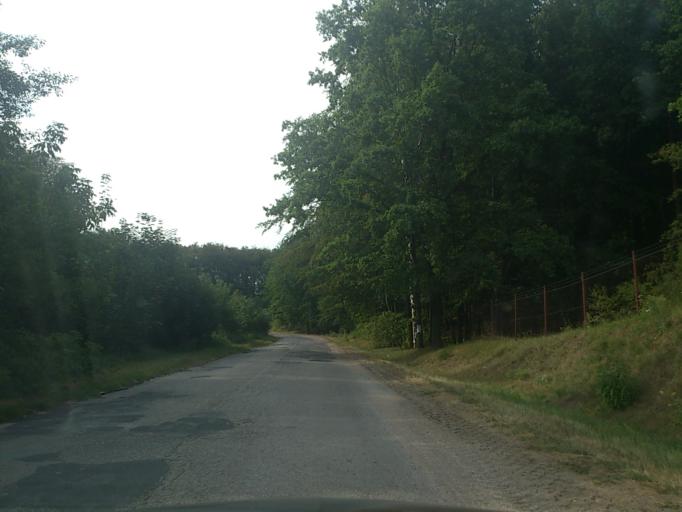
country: PL
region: Kujawsko-Pomorskie
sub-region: Powiat golubsko-dobrzynski
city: Golub-Dobrzyn
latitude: 53.1122
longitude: 19.0416
